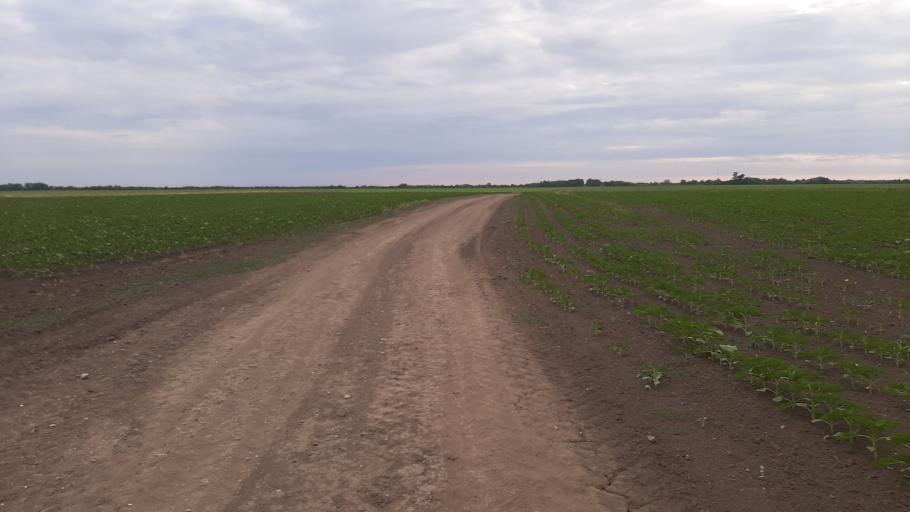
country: HU
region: Csongrad
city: Deszk
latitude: 46.1738
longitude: 20.2179
